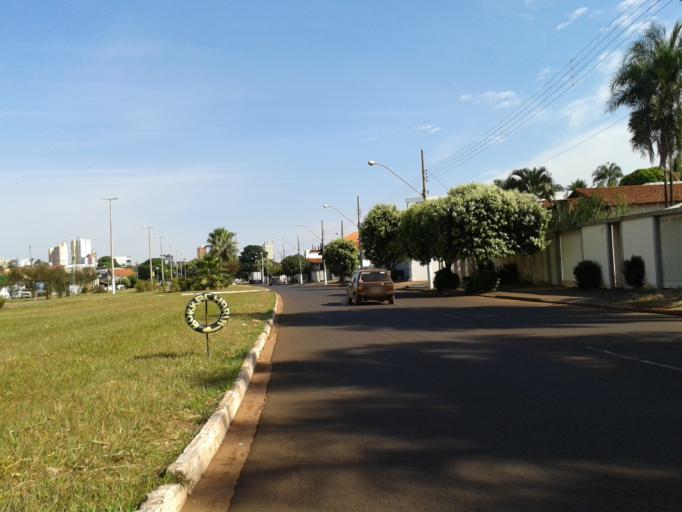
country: BR
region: Minas Gerais
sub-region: Ituiutaba
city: Ituiutaba
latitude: -18.9729
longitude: -49.4519
